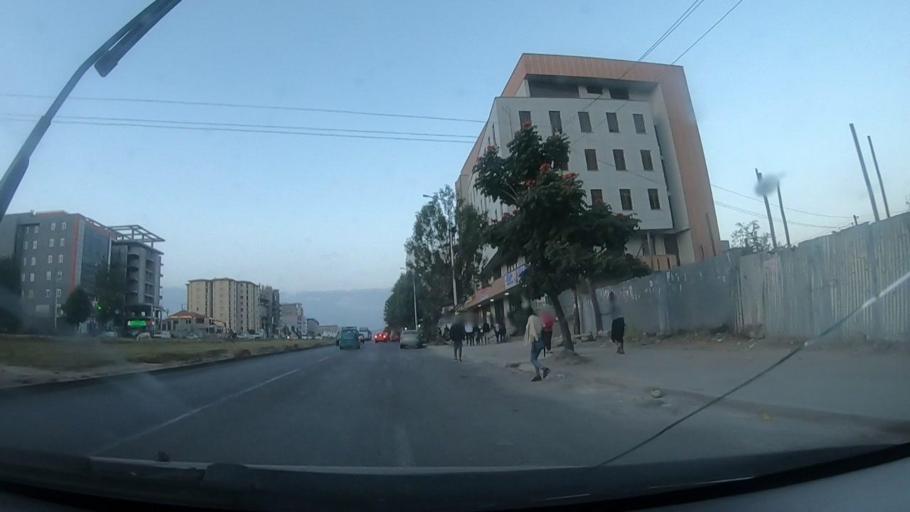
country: ET
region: Adis Abeba
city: Addis Ababa
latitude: 9.0280
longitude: 38.8781
